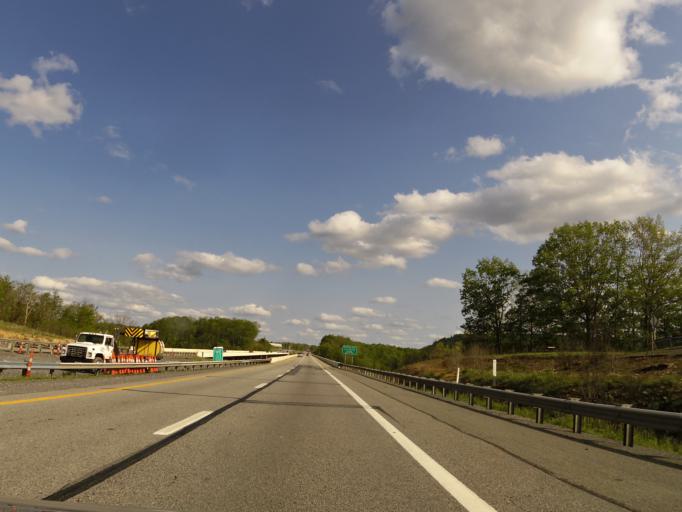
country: US
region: West Virginia
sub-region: Mercer County
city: Athens
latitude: 37.4815
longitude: -81.0752
